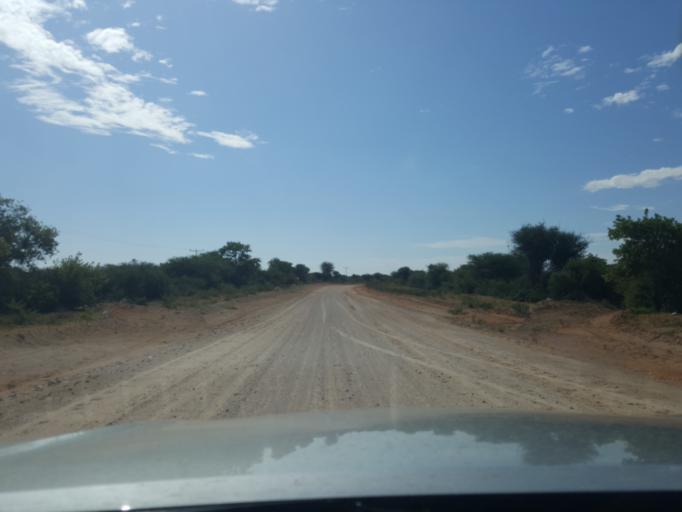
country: BW
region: Kweneng
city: Khudumelapye
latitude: -23.7792
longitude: 24.7721
